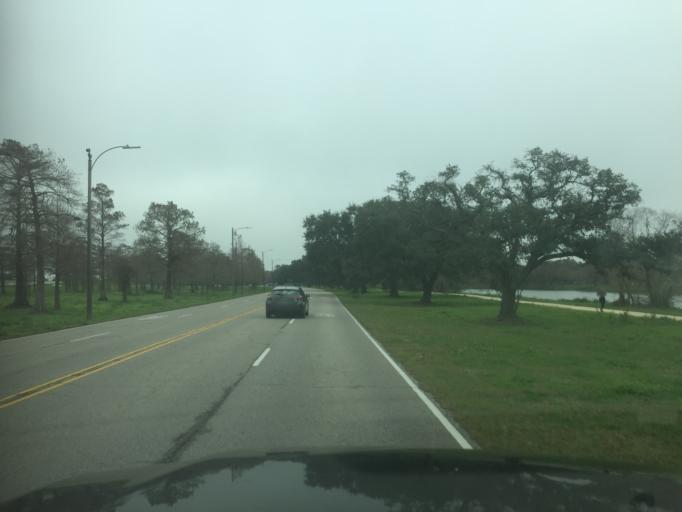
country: US
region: Louisiana
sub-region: Jefferson Parish
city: Metairie
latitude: 30.0154
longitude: -90.0973
